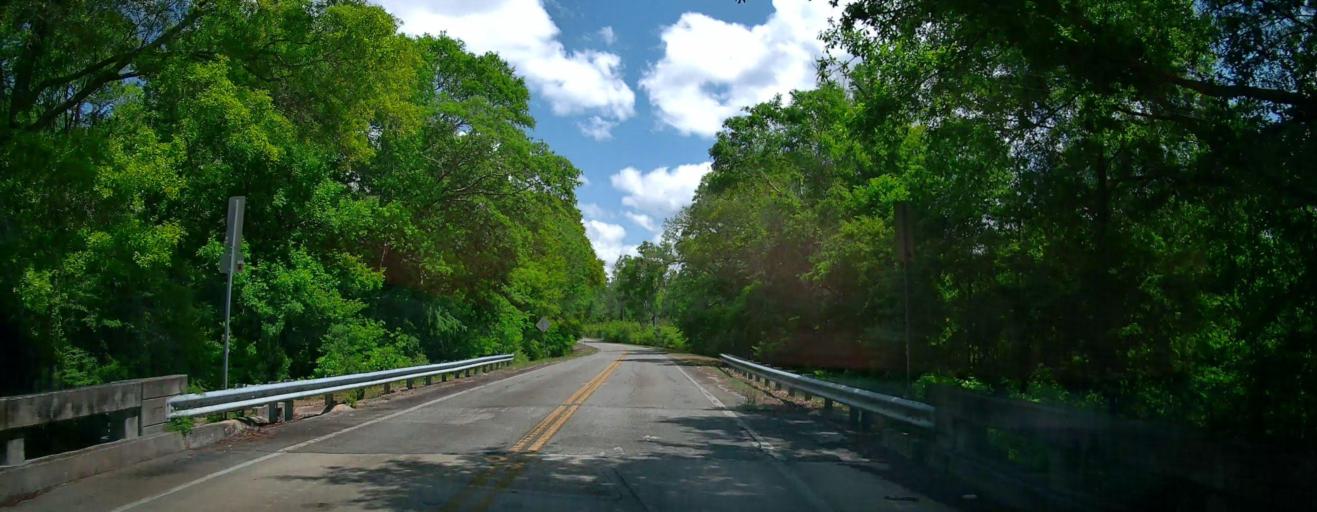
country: US
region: Georgia
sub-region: Bleckley County
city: Cochran
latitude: 32.4652
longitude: -83.2814
